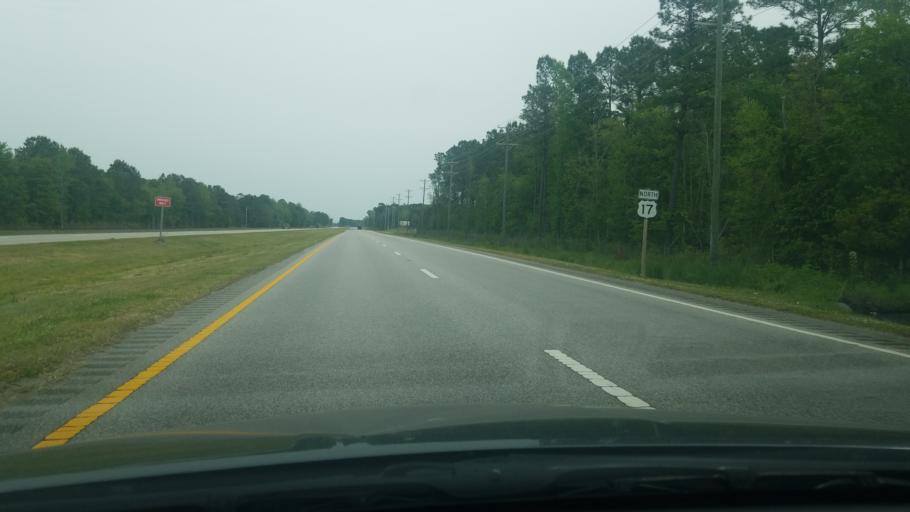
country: US
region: North Carolina
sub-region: Beaufort County
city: Washington
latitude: 35.4594
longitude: -77.1212
